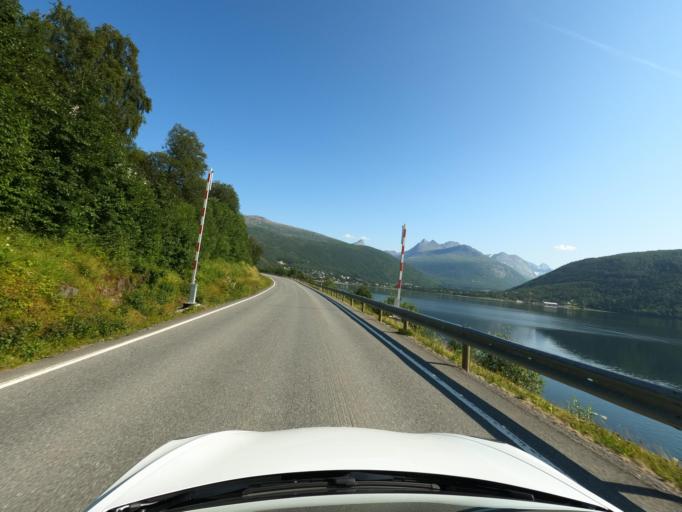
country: NO
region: Nordland
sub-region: Narvik
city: Narvik
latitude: 68.3850
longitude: 17.5670
